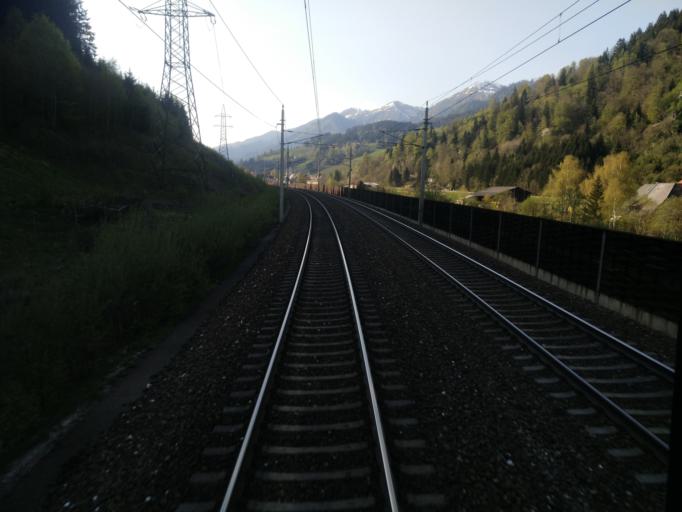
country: AT
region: Styria
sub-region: Politischer Bezirk Leoben
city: Wald am Schoberpass
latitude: 47.4430
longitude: 14.6838
